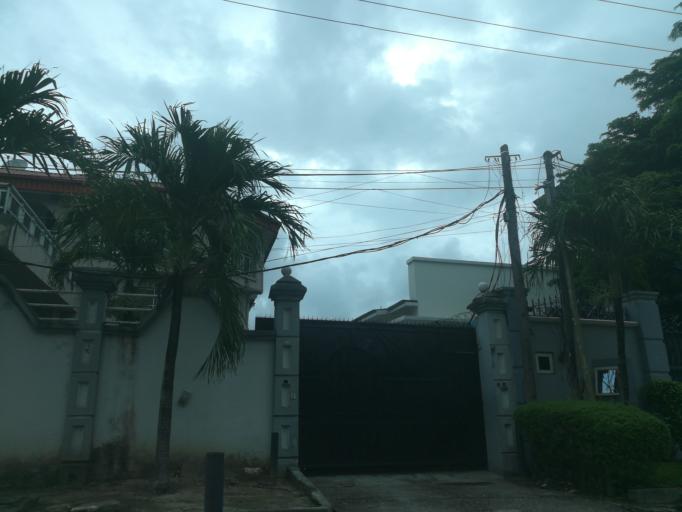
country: NG
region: Lagos
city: Ikoyi
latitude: 6.4252
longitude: 3.4221
